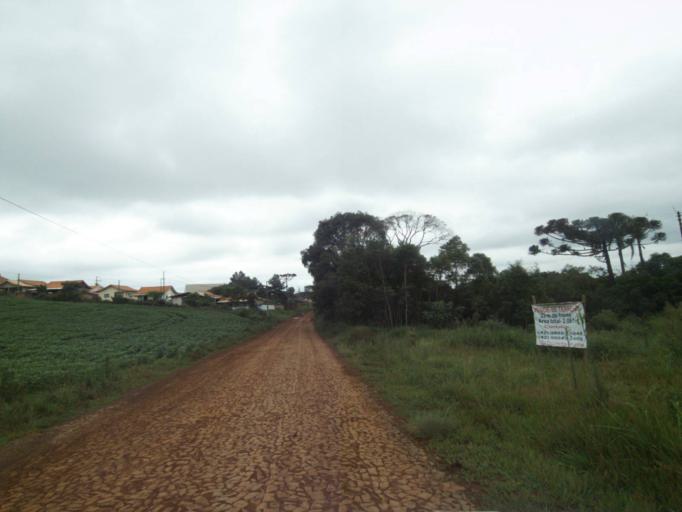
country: BR
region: Parana
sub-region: Pitanga
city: Pitanga
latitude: -24.9377
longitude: -51.8668
